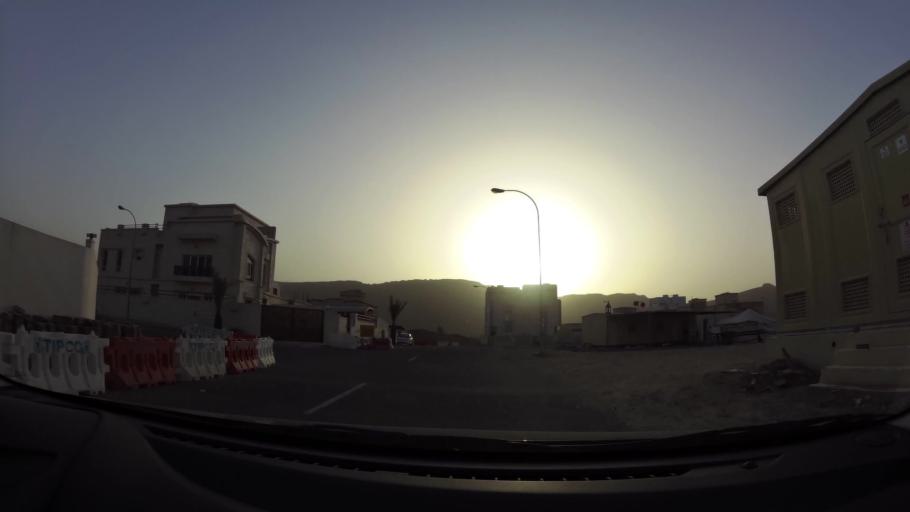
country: OM
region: Muhafazat Masqat
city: Bawshar
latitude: 23.4989
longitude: 58.3191
